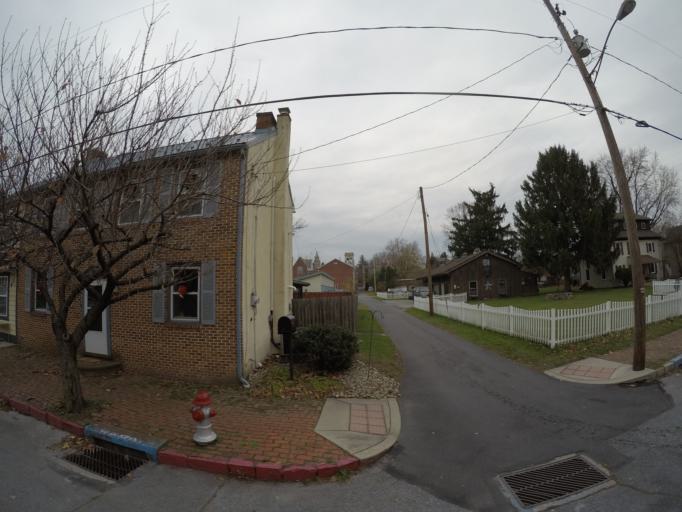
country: US
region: Pennsylvania
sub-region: Lancaster County
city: Marietta
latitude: 40.0551
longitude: -76.5553
